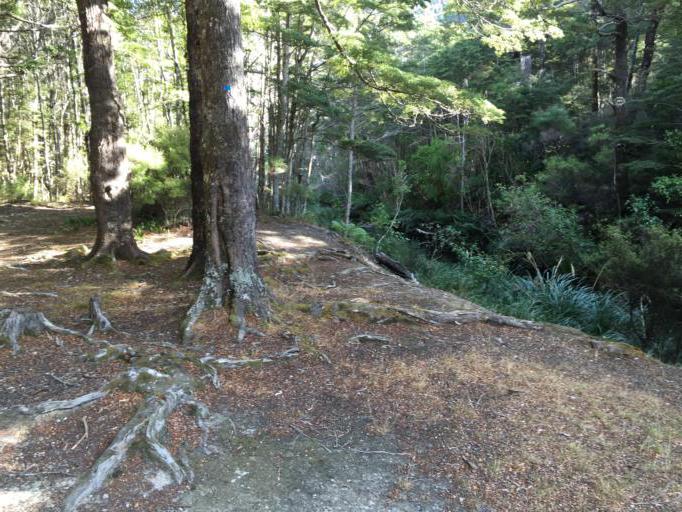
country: NZ
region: Wellington
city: Petone
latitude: -41.3124
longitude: 174.9004
